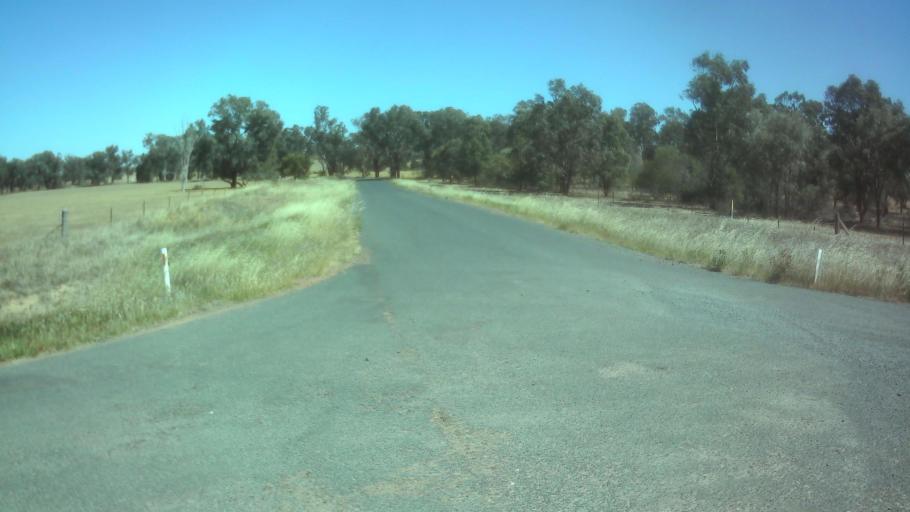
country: AU
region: New South Wales
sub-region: Weddin
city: Grenfell
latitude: -33.9875
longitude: 148.4116
